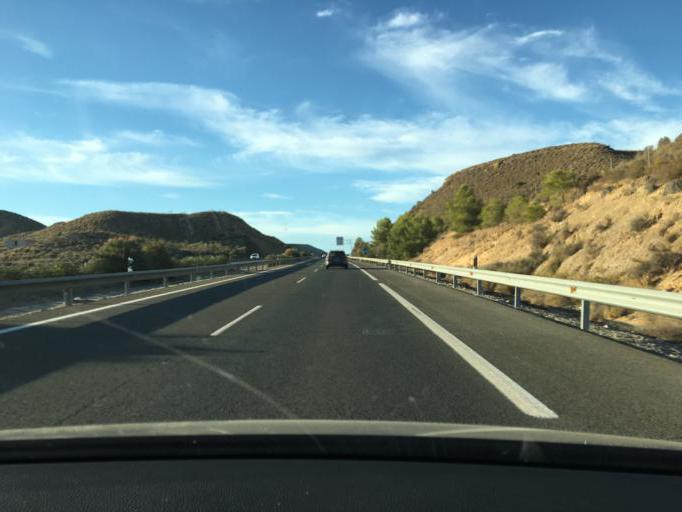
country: ES
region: Andalusia
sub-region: Provincia de Almeria
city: Sorbas
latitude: 37.0605
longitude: -2.0522
